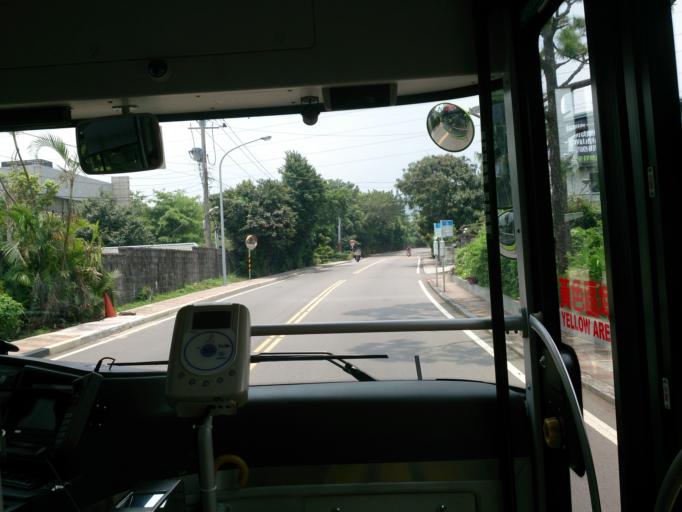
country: TW
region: Taipei
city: Taipei
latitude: 25.1066
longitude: 121.5452
